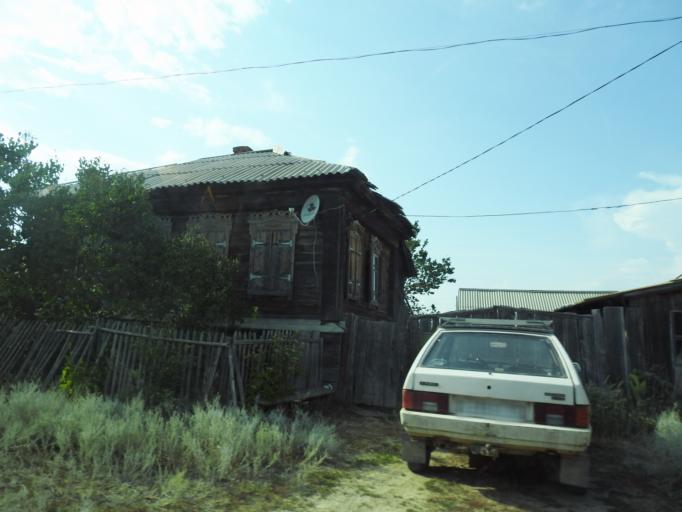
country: RU
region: Saratov
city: Rovnoye
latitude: 50.5102
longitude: 45.7623
